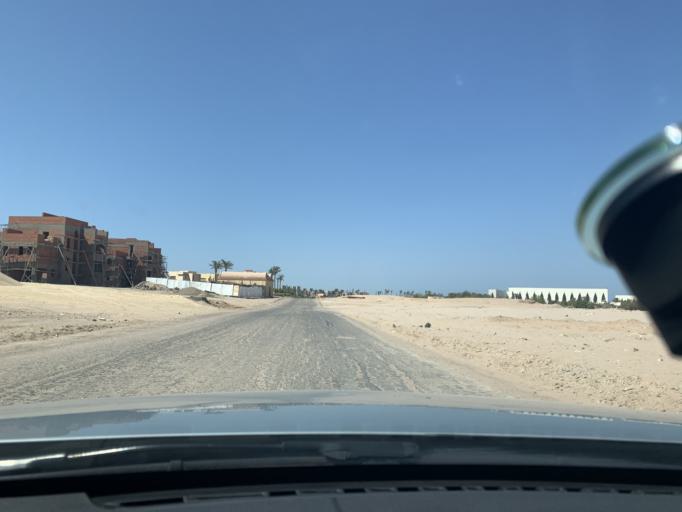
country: EG
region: Red Sea
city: El Gouna
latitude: 27.4004
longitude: 33.6633
